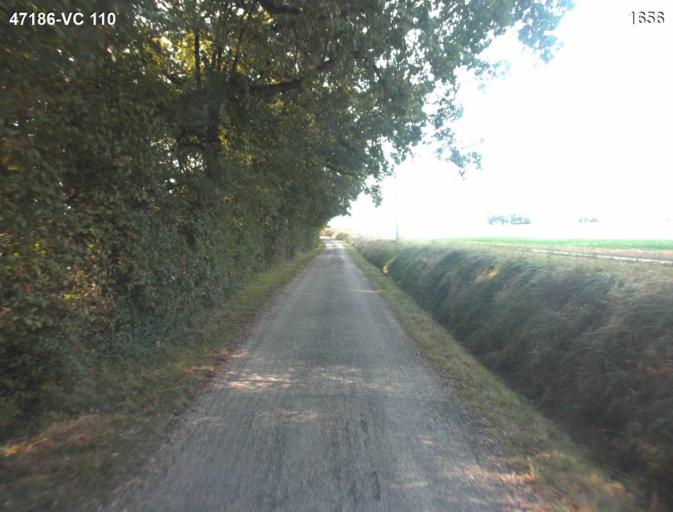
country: FR
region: Aquitaine
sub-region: Departement du Lot-et-Garonne
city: Port-Sainte-Marie
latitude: 44.1855
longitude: 0.4301
